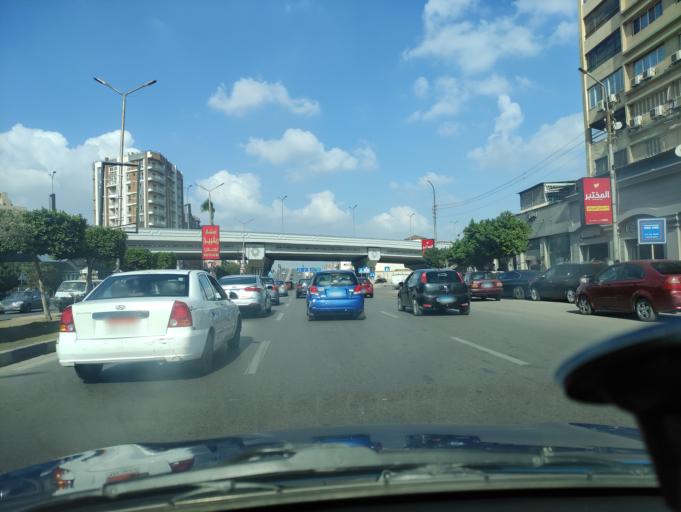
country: EG
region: Muhafazat al Qahirah
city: Cairo
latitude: 30.0899
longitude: 31.3415
